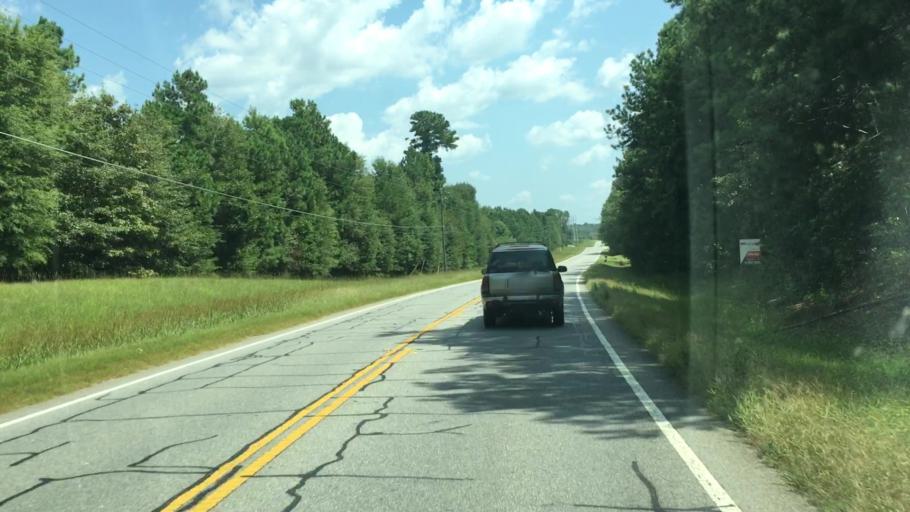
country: US
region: Georgia
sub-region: Barrow County
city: Statham
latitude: 33.9074
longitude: -83.5840
